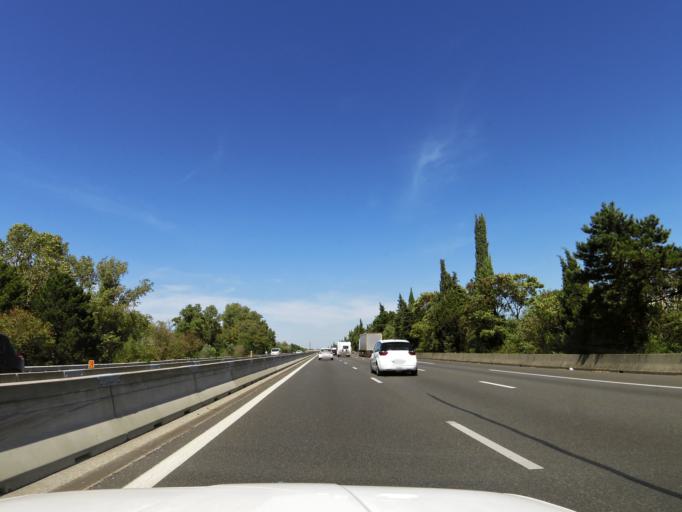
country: FR
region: Rhone-Alpes
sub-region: Departement de la Drome
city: Etoile-sur-Rhone
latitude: 44.8362
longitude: 4.8626
